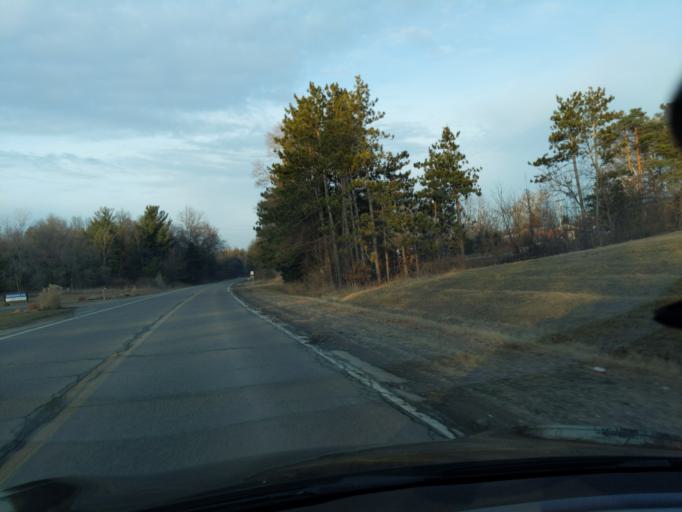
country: US
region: Michigan
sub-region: Livingston County
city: Brighton
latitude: 42.5950
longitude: -83.7535
